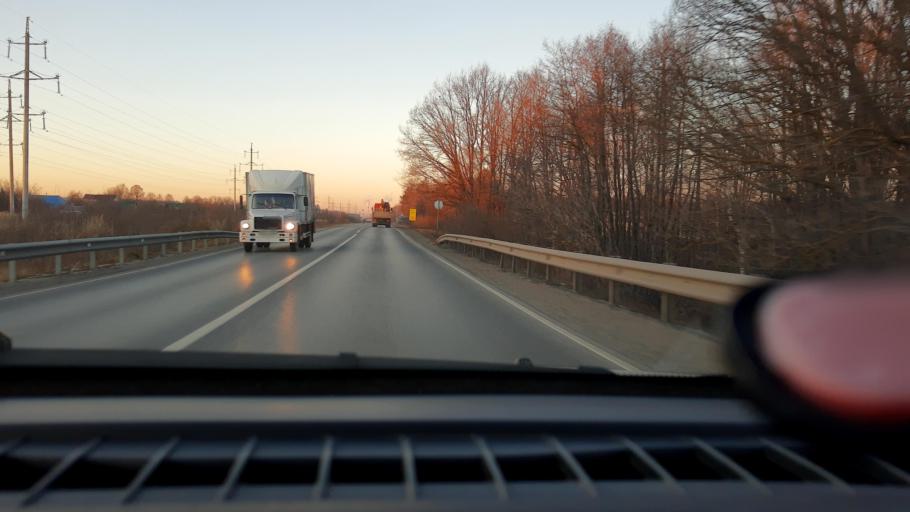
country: RU
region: Nizjnij Novgorod
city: Lukino
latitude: 56.4488
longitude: 43.6329
